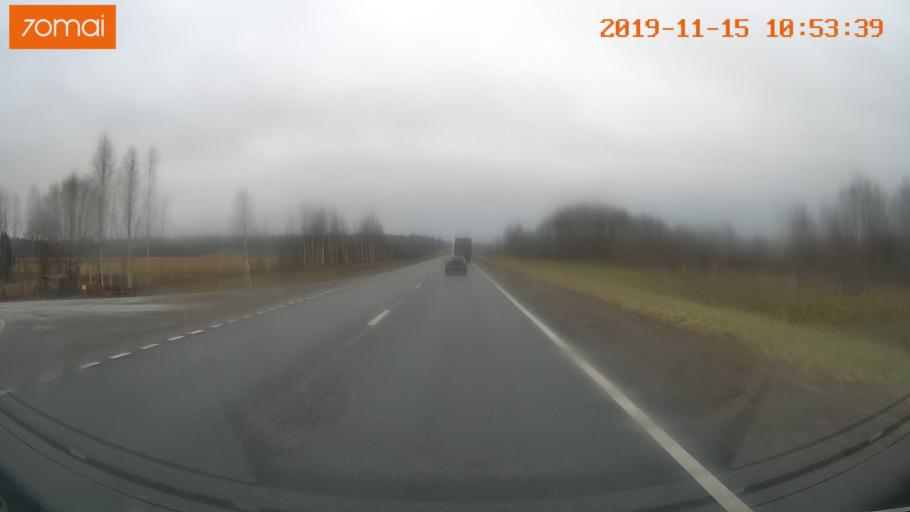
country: RU
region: Vologda
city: Chebsara
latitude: 59.1681
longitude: 38.7594
